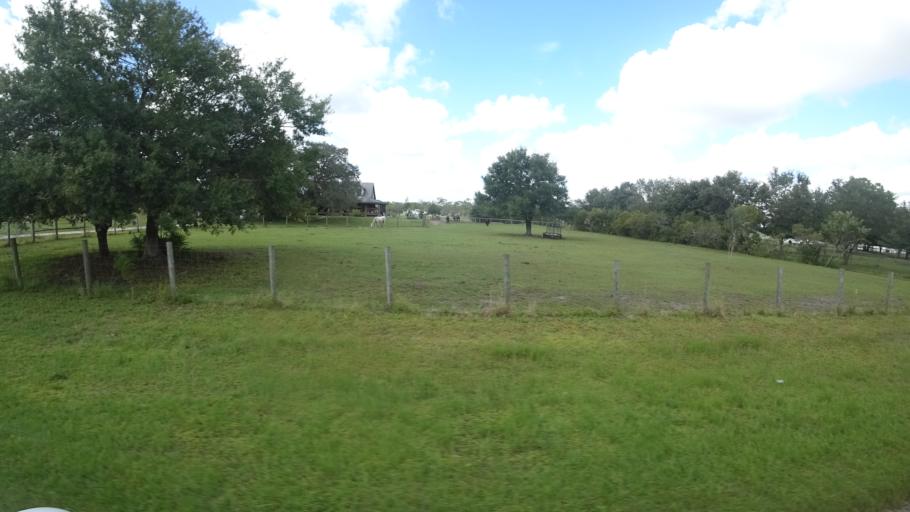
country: US
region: Florida
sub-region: Sarasota County
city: Lake Sarasota
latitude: 27.4020
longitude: -82.2711
